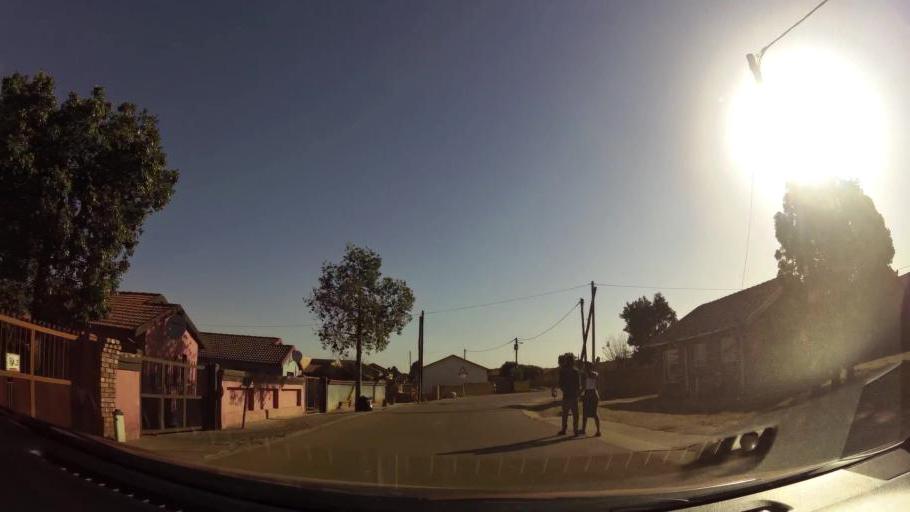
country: ZA
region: Gauteng
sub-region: City of Tshwane Metropolitan Municipality
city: Mabopane
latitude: -25.5868
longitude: 28.1092
